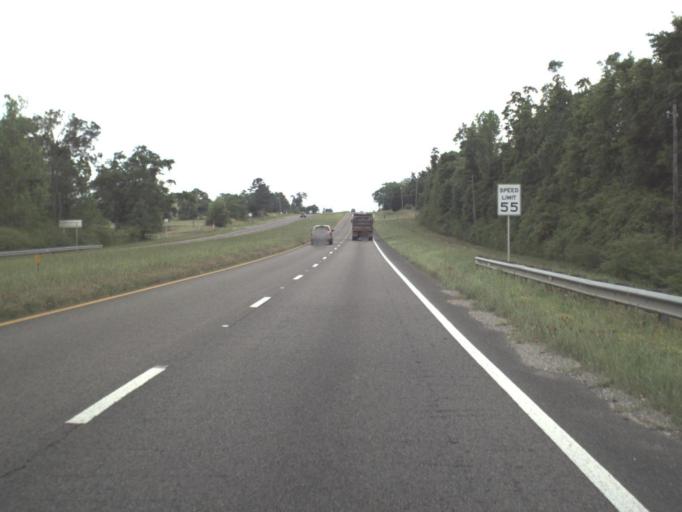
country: US
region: Florida
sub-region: Escambia County
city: Molino
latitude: 30.7158
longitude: -87.3500
